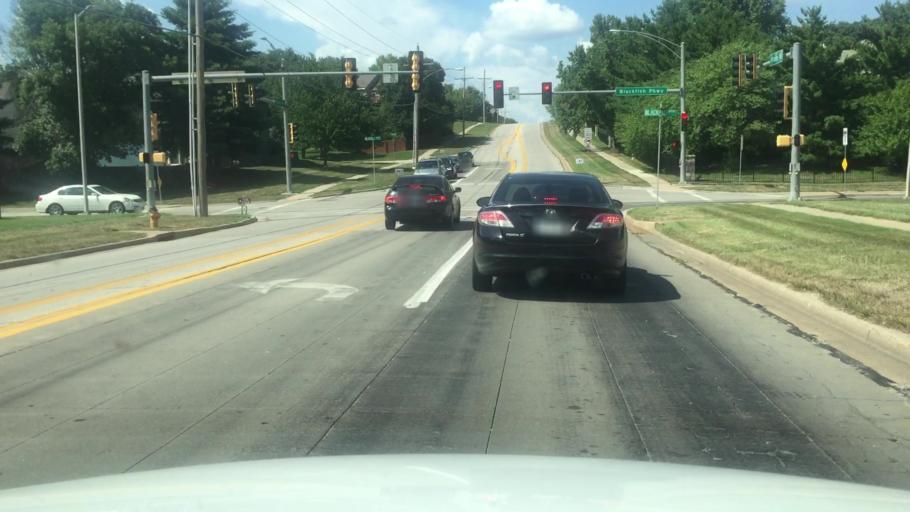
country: US
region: Kansas
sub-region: Johnson County
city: Lenexa
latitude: 38.9950
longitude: -94.7423
